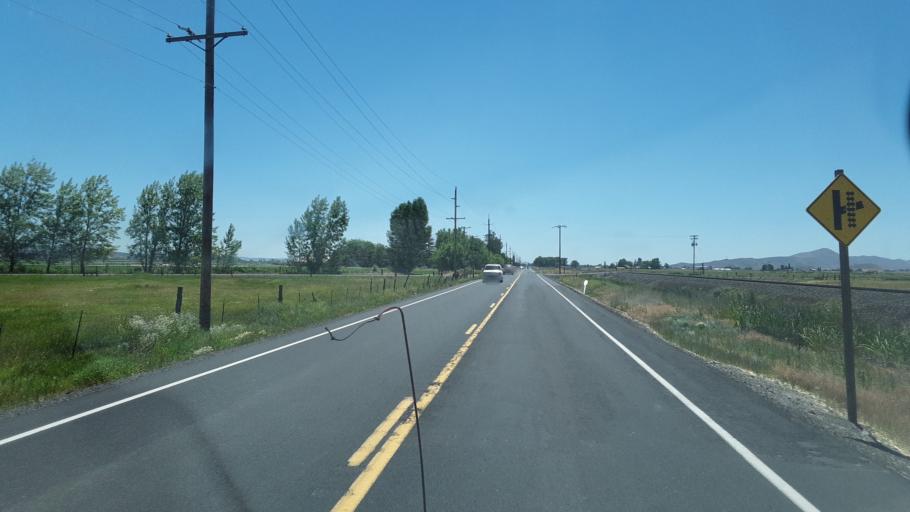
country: US
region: Oregon
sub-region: Klamath County
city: Altamont
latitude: 42.0529
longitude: -121.6412
